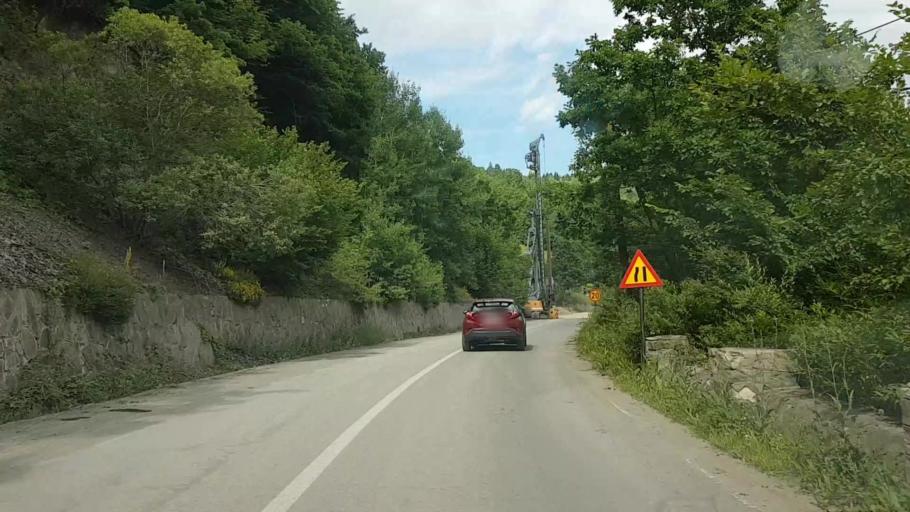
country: RO
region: Neamt
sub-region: Comuna Hangu
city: Hangu
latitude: 47.0463
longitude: 26.0441
